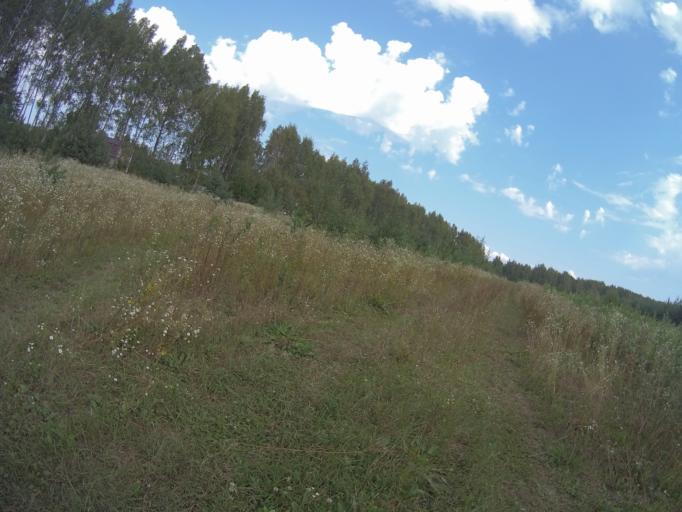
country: RU
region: Vladimir
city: Raduzhnyy
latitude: 56.0002
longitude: 40.2805
